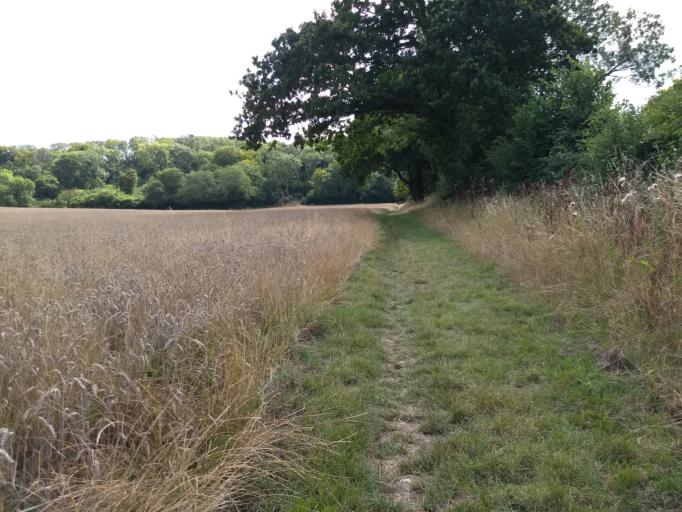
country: GB
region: England
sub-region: Isle of Wight
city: Brading
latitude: 50.6816
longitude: -1.1506
